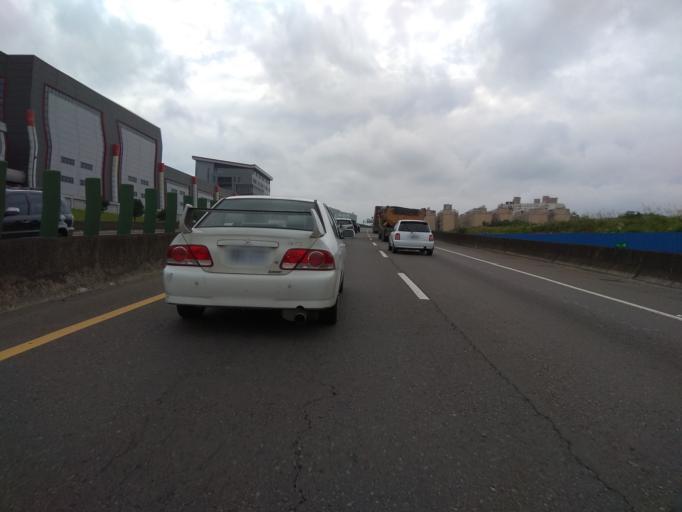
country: TW
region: Taiwan
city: Taoyuan City
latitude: 24.9525
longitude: 121.1583
